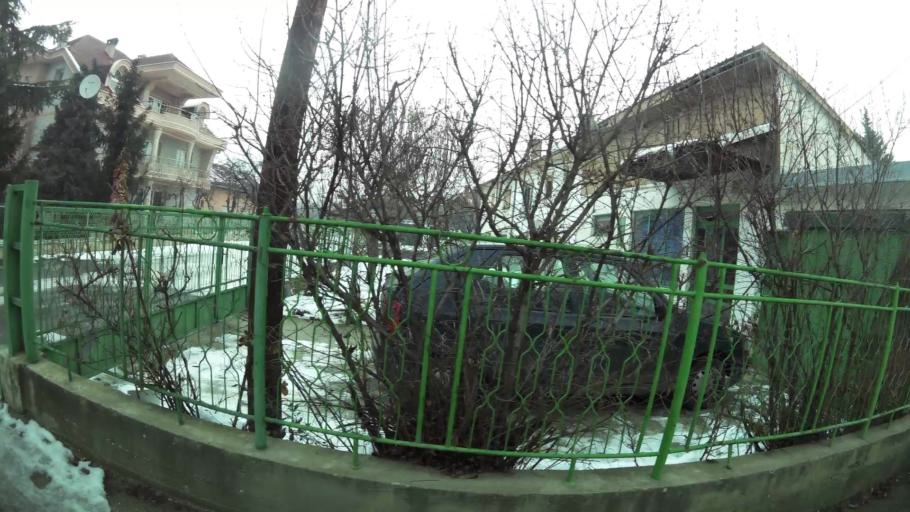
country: MK
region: Saraj
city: Saraj
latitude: 42.0343
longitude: 21.3541
